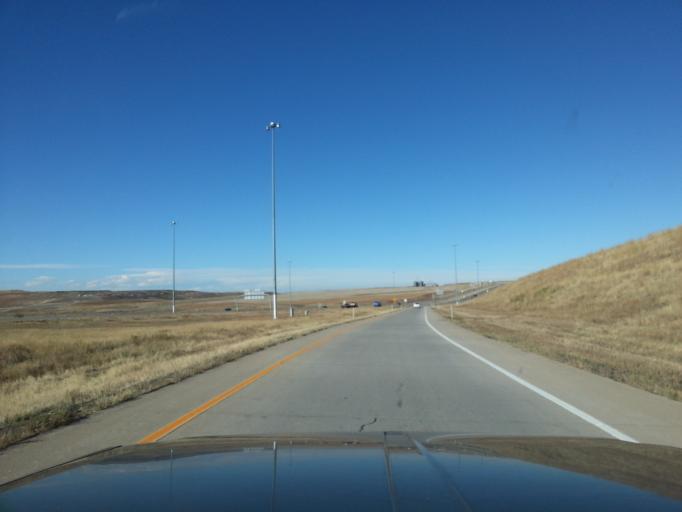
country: US
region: Colorado
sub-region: Adams County
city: Aurora
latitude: 39.8389
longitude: -104.7460
